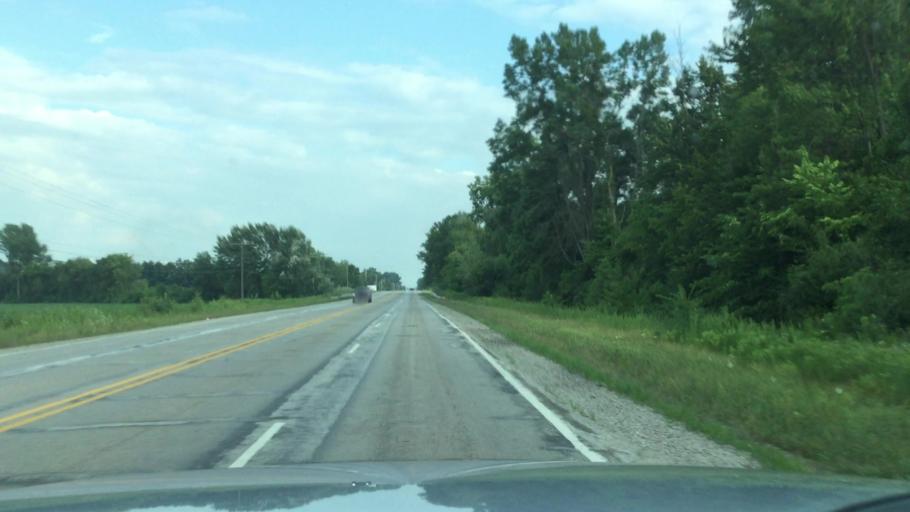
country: US
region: Michigan
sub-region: Saginaw County
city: Birch Run
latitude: 43.2715
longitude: -83.7855
